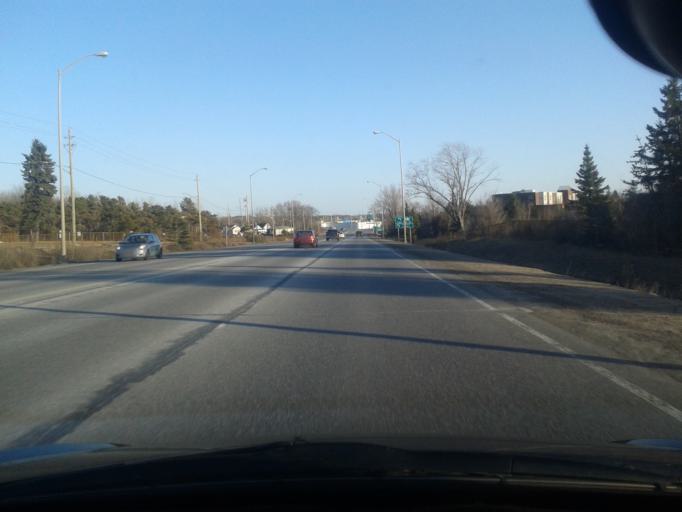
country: CA
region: Ontario
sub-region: Nipissing District
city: North Bay
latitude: 46.3229
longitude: -79.4470
